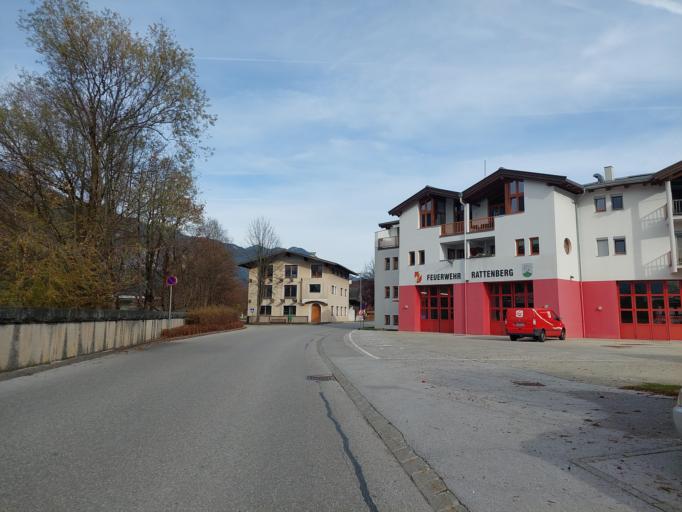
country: AT
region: Tyrol
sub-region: Politischer Bezirk Kufstein
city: Rattenberg
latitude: 47.4427
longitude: 11.8955
